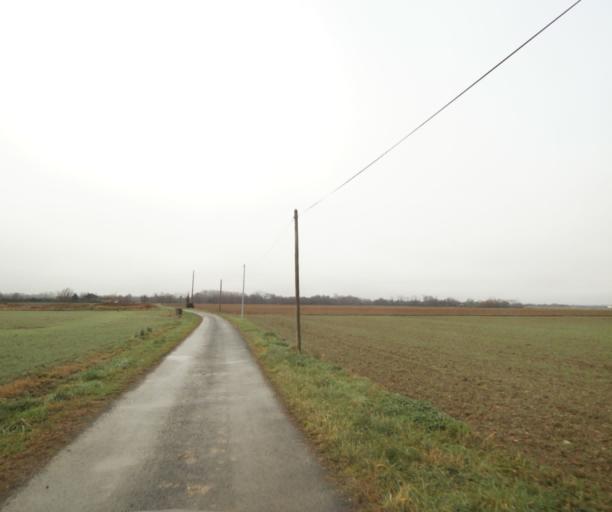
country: FR
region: Midi-Pyrenees
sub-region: Departement du Tarn-et-Garonne
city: Nohic
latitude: 43.8870
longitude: 1.4704
